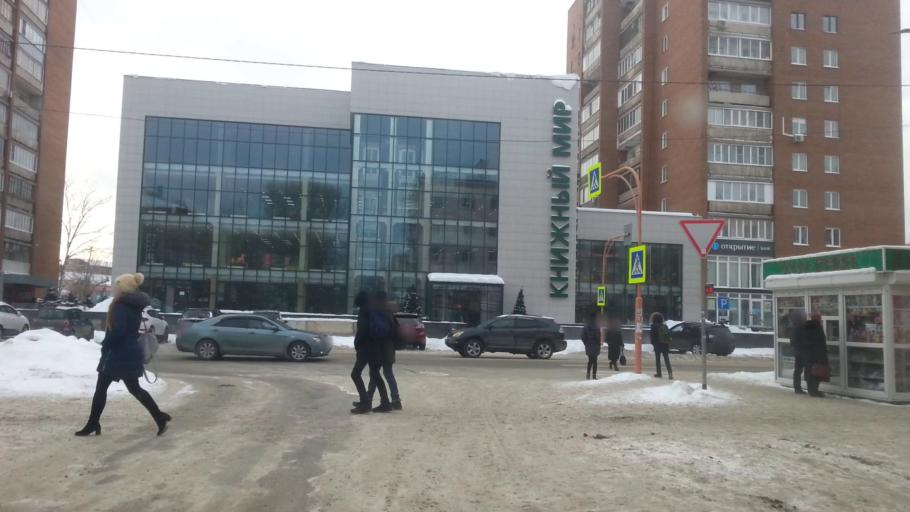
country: RU
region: Altai Krai
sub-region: Gorod Barnaulskiy
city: Barnaul
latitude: 53.3492
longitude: 83.7661
